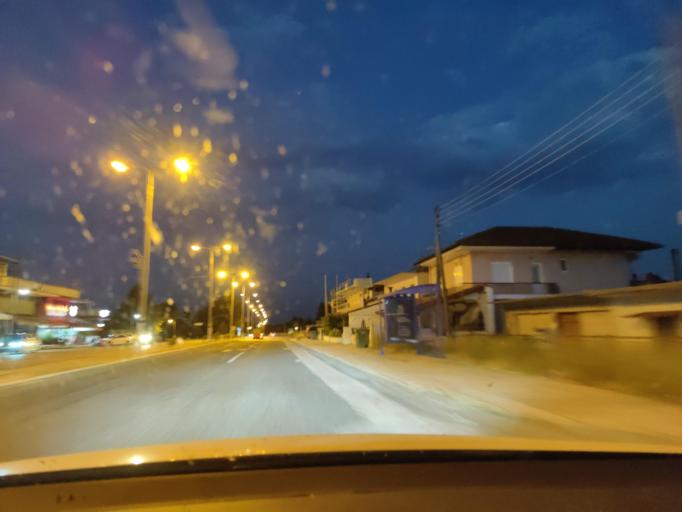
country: GR
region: Central Macedonia
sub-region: Nomos Serron
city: Lefkonas
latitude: 41.0962
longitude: 23.5014
